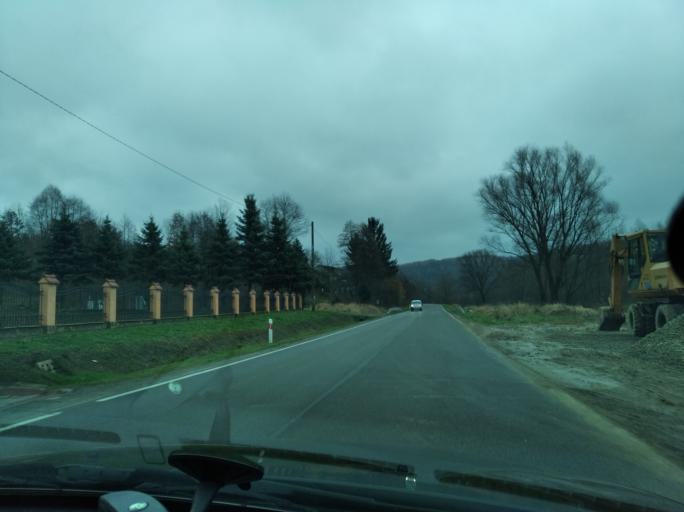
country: PL
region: Subcarpathian Voivodeship
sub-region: Powiat przeworski
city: Manasterz
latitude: 49.9223
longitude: 22.3112
